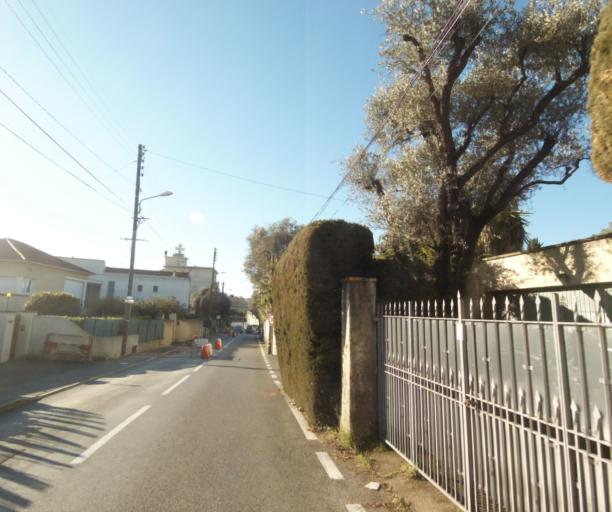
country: FR
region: Provence-Alpes-Cote d'Azur
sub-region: Departement des Alpes-Maritimes
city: Antibes
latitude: 43.5790
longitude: 7.1057
